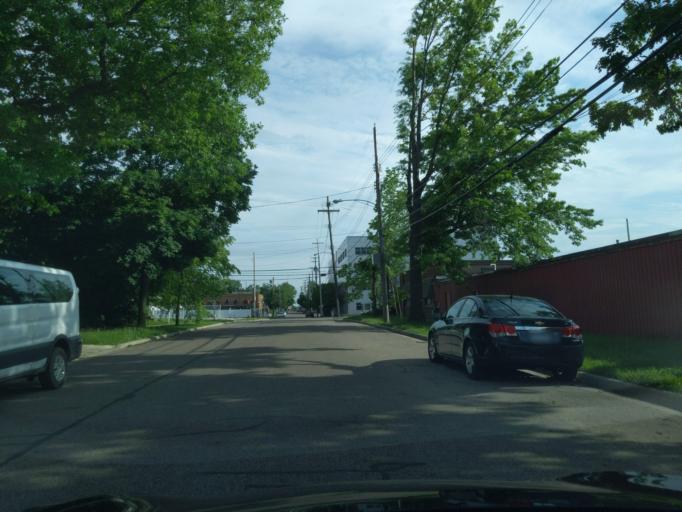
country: US
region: Michigan
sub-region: Ingham County
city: Lansing
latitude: 42.7353
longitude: -84.5411
